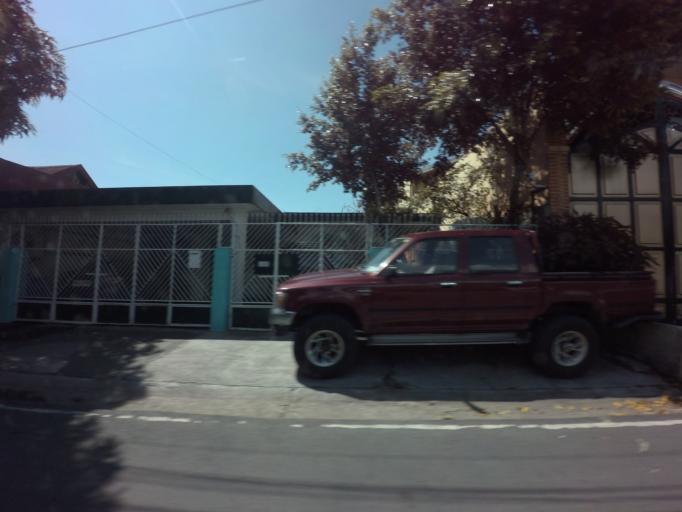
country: PH
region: Calabarzon
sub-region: Province of Rizal
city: Las Pinas
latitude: 14.4423
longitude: 120.9874
